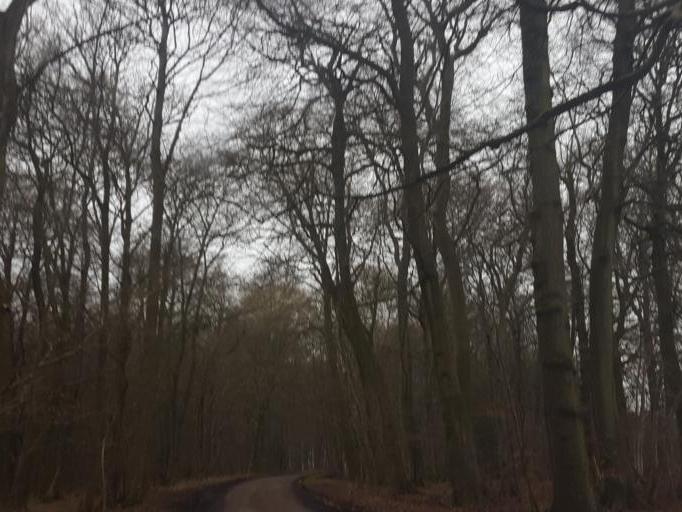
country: GB
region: England
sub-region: Buckinghamshire
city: Stokenchurch
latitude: 51.6644
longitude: -0.9339
